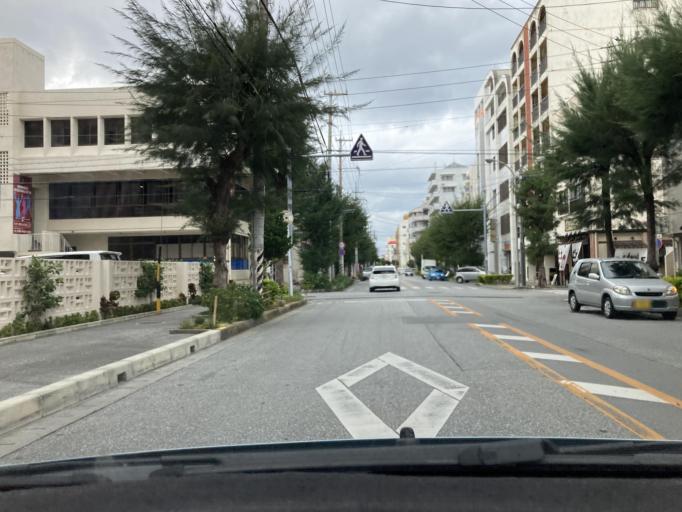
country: JP
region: Okinawa
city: Naha-shi
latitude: 26.2145
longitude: 127.6728
